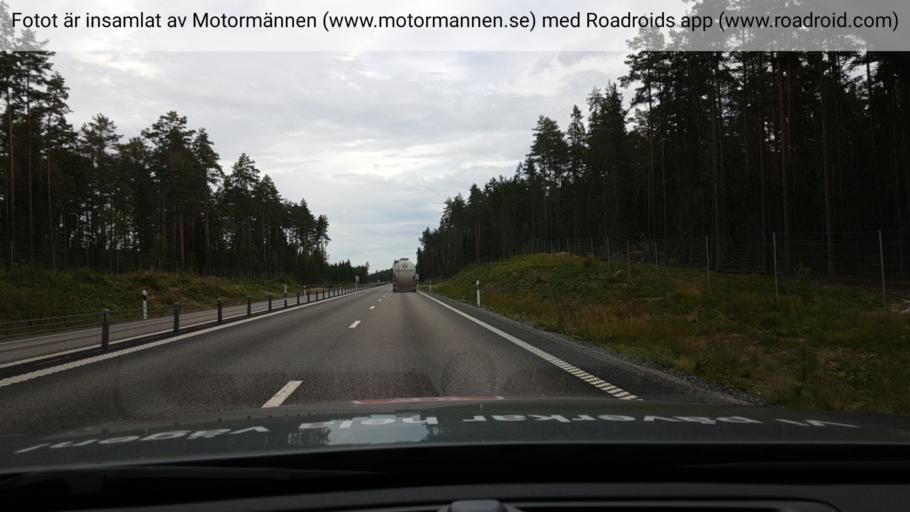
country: SE
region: Uppsala
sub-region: Heby Kommun
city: Tarnsjo
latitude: 60.0679
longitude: 16.9050
